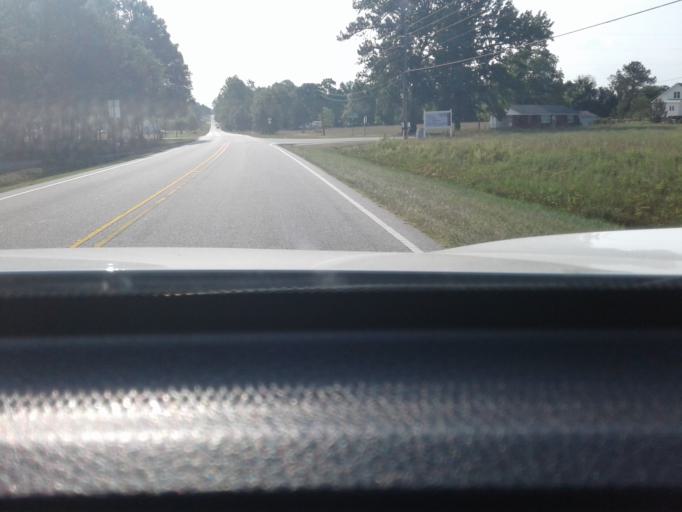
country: US
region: North Carolina
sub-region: Johnston County
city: Benson
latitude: 35.3900
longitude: -78.5820
